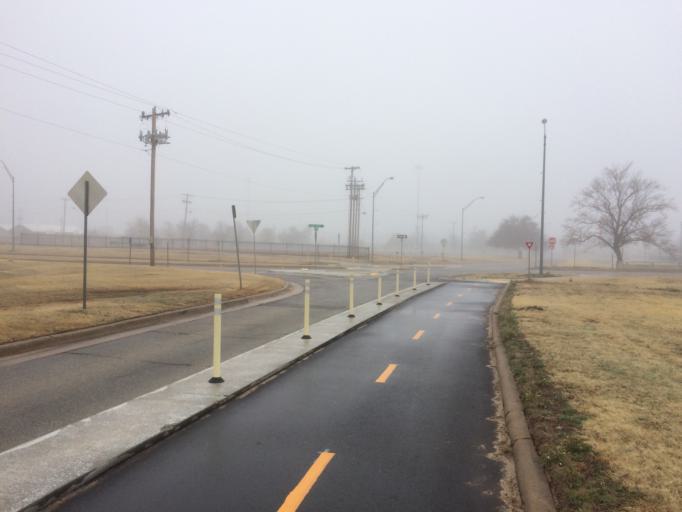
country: US
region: Oklahoma
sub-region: Oklahoma County
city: Oklahoma City
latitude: 35.4773
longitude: -97.5758
